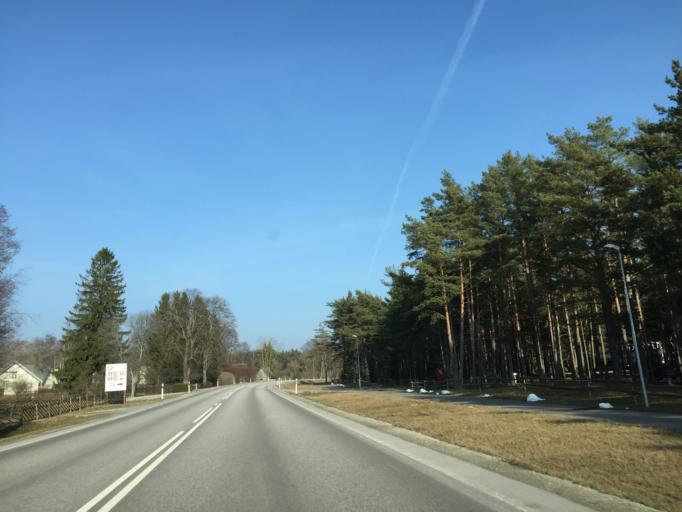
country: EE
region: Saare
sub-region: Kuressaare linn
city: Kuressaare
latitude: 58.2183
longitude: 22.3302
